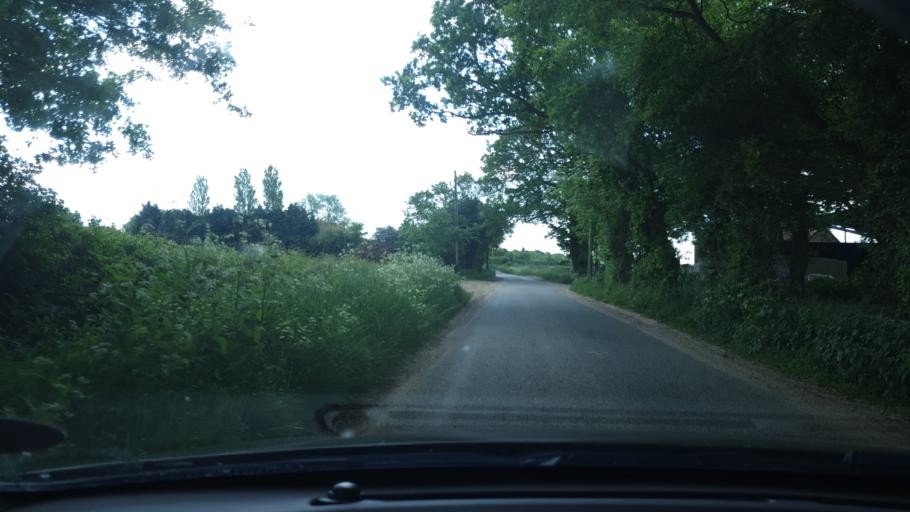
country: GB
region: England
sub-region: Essex
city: Great Bentley
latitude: 51.8442
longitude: 1.0904
